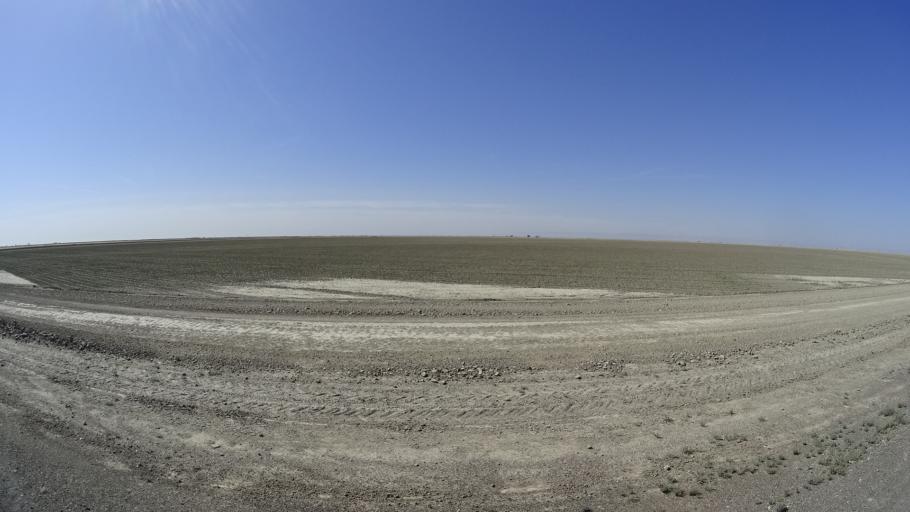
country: US
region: California
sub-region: Tulare County
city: Alpaugh
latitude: 35.8914
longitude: -119.5492
